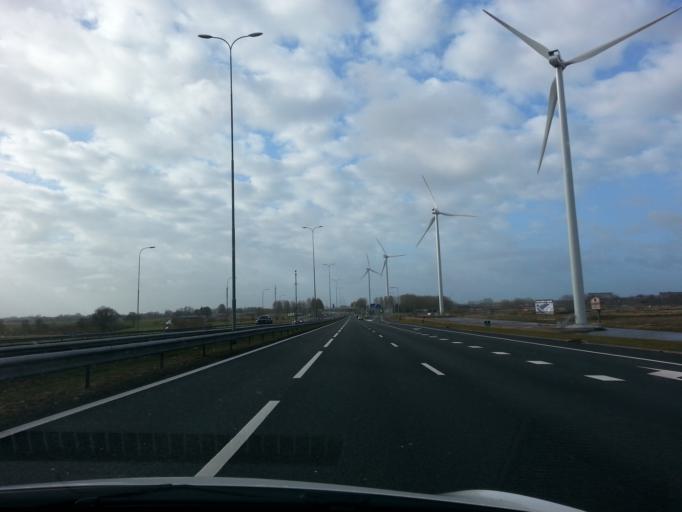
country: NL
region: Utrecht
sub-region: Gemeente Utrecht
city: Lunetten
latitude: 52.0216
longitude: 5.1272
